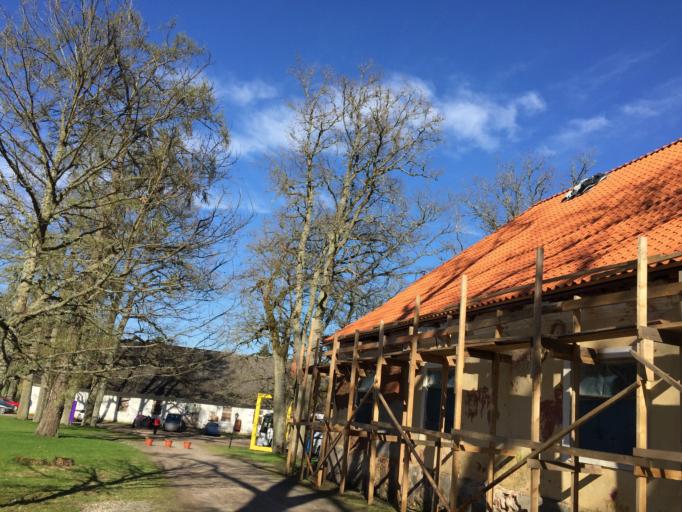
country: EE
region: Vorumaa
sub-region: Antsla vald
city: Vana-Antsla
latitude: 57.9018
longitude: 26.2809
